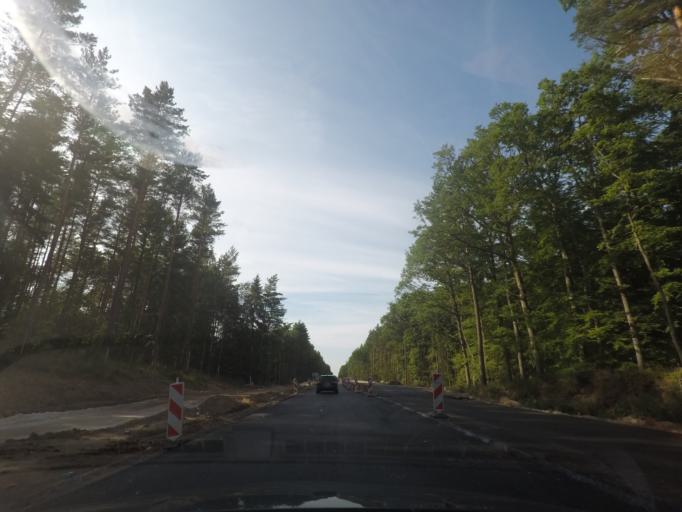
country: PL
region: Pomeranian Voivodeship
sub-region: Powiat leborski
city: Leba
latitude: 54.7009
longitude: 17.5871
